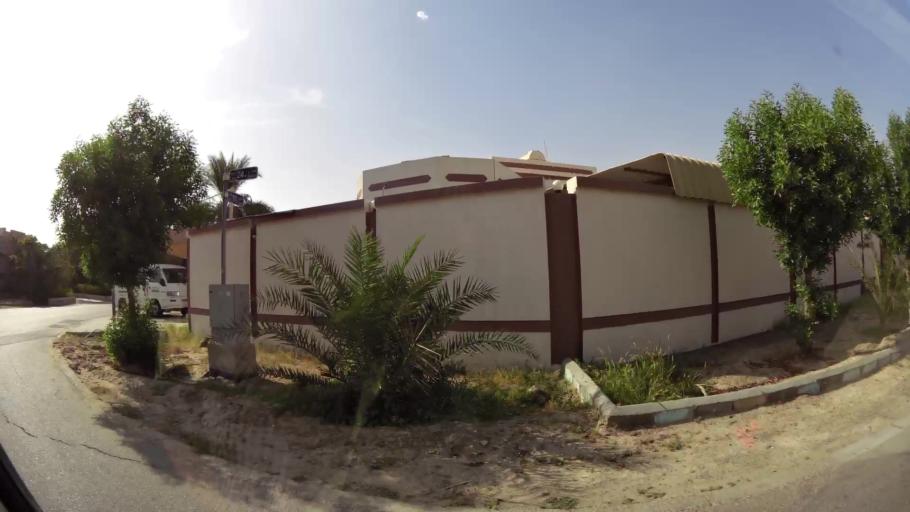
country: AE
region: Ash Shariqah
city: Sharjah
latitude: 25.2605
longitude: 55.3974
